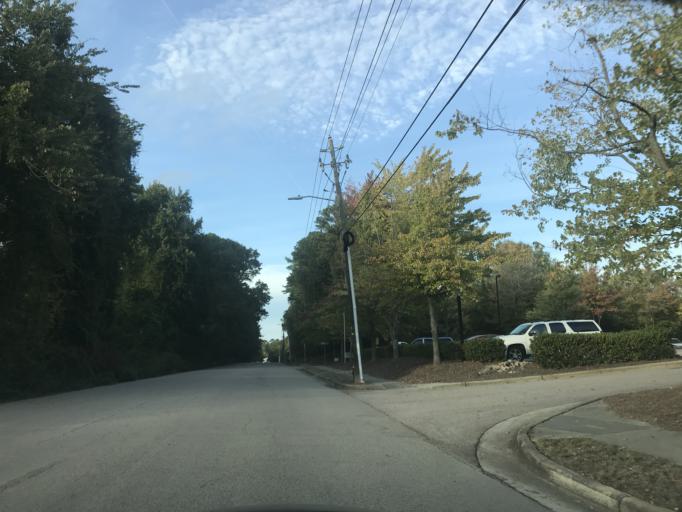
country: US
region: North Carolina
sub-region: Wake County
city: Raleigh
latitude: 35.8301
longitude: -78.6124
